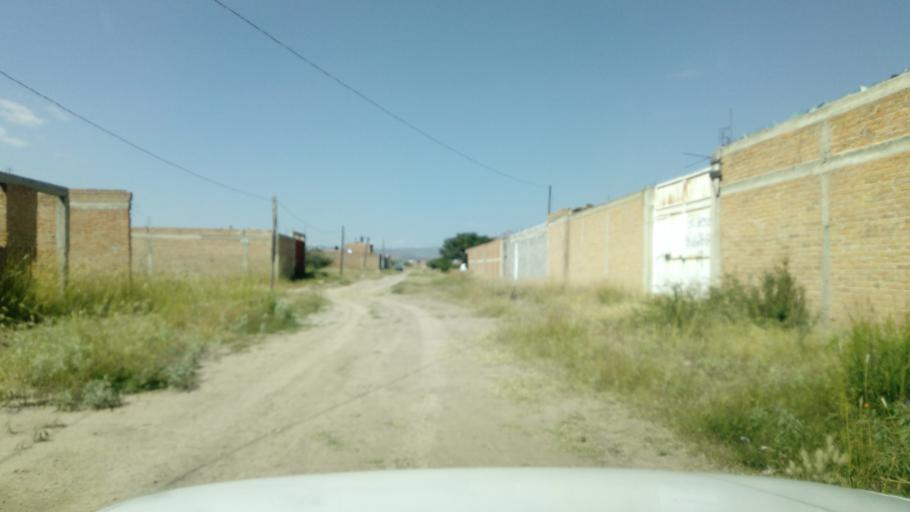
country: MX
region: Durango
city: Victoria de Durango
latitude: 23.9826
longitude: -104.6711
